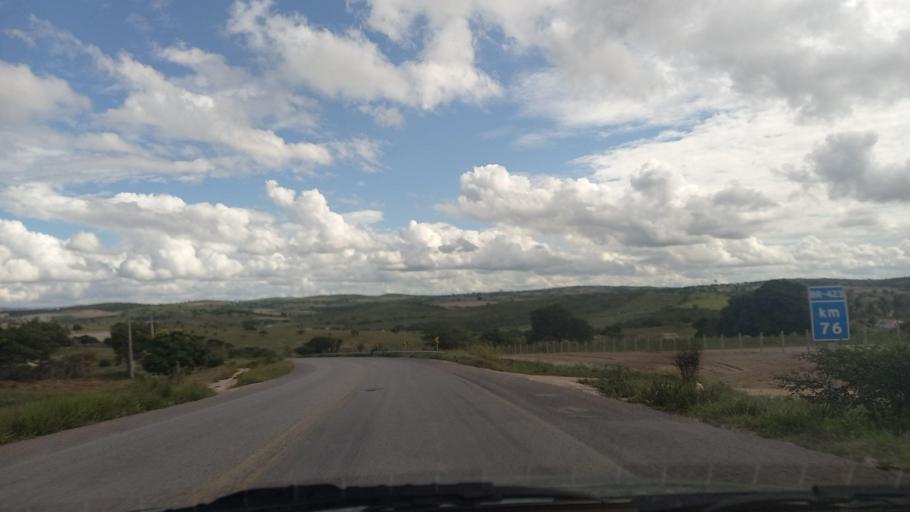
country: BR
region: Pernambuco
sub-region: Lajedo
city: Lajedo
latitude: -8.7265
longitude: -36.4310
